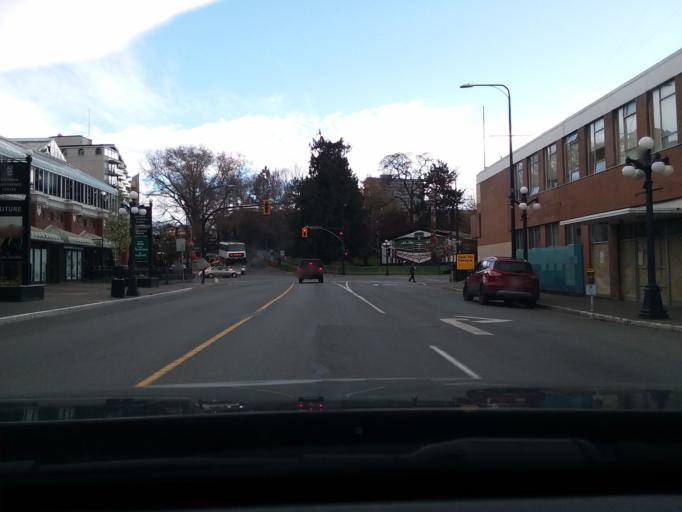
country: CA
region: British Columbia
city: Victoria
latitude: 48.4208
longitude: -123.3662
